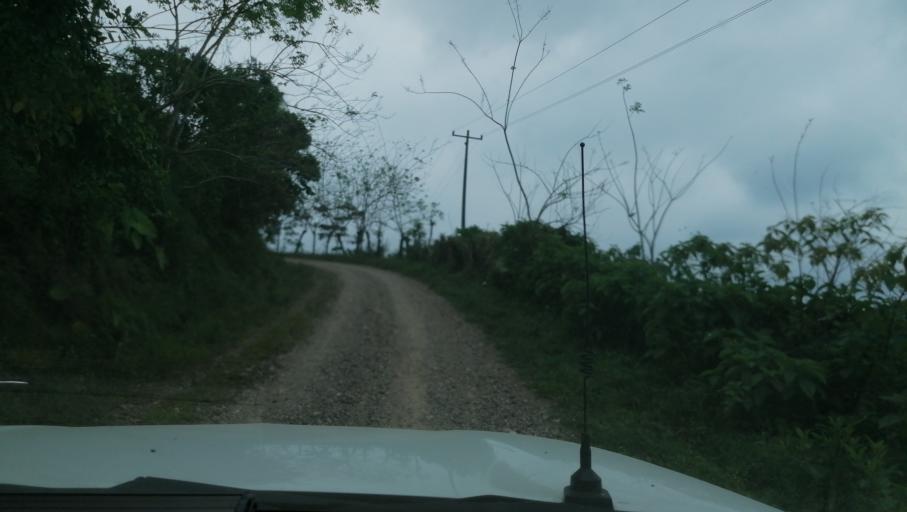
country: MX
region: Chiapas
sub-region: Francisco Leon
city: San Miguel la Sardina
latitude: 17.3348
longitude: -93.3133
